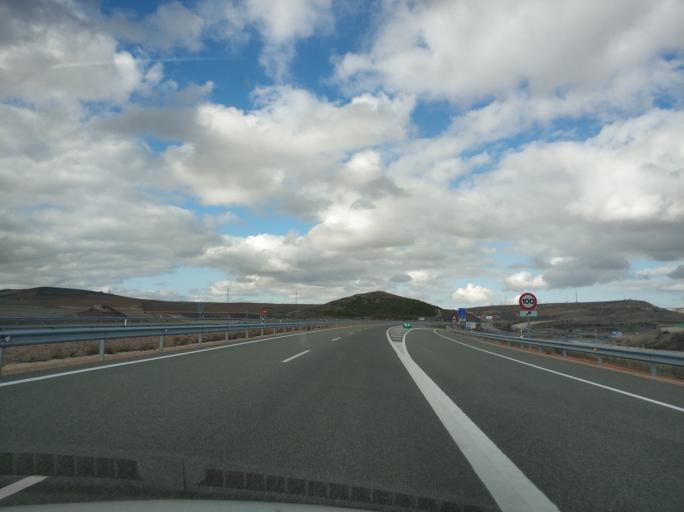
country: ES
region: Castille and Leon
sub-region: Provincia de Soria
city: Yelo
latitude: 41.2159
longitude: -2.4696
